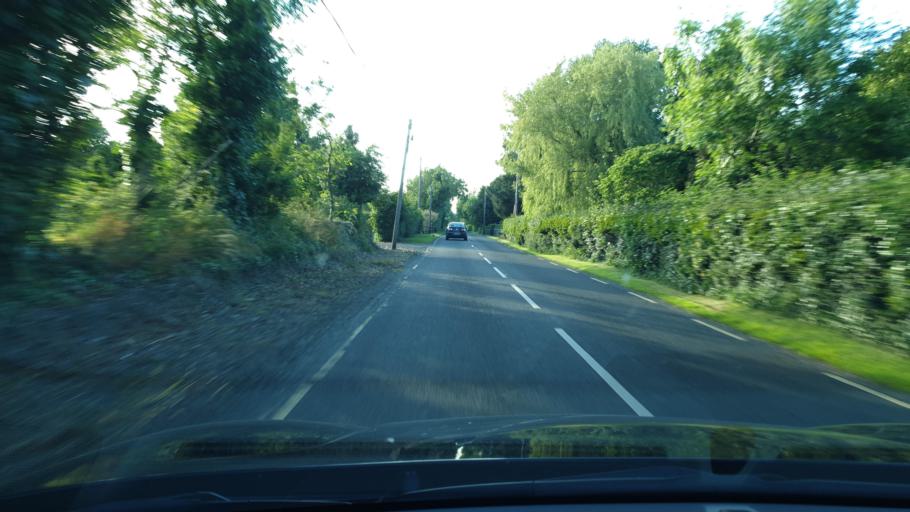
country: IE
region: Leinster
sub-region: An Mhi
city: Ashbourne
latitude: 53.4735
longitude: -6.4232
